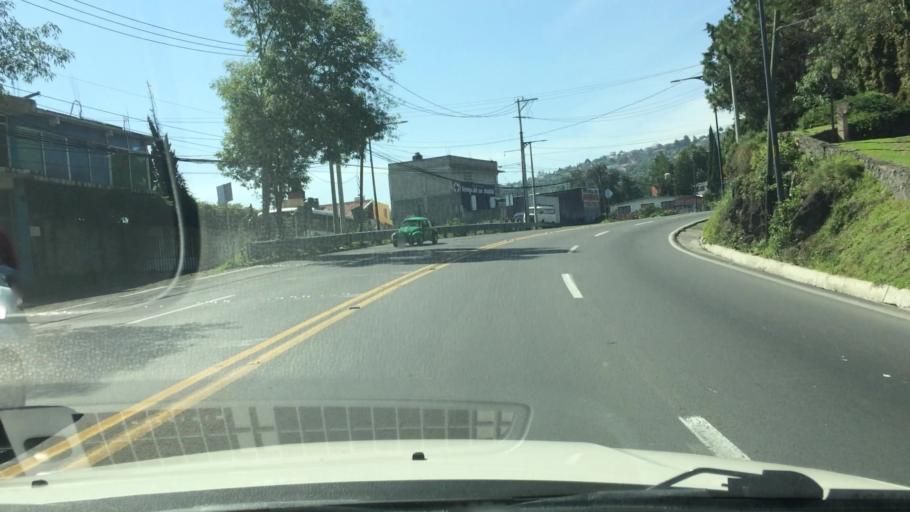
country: MX
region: Mexico City
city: Tlalpan
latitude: 19.2473
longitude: -99.1715
